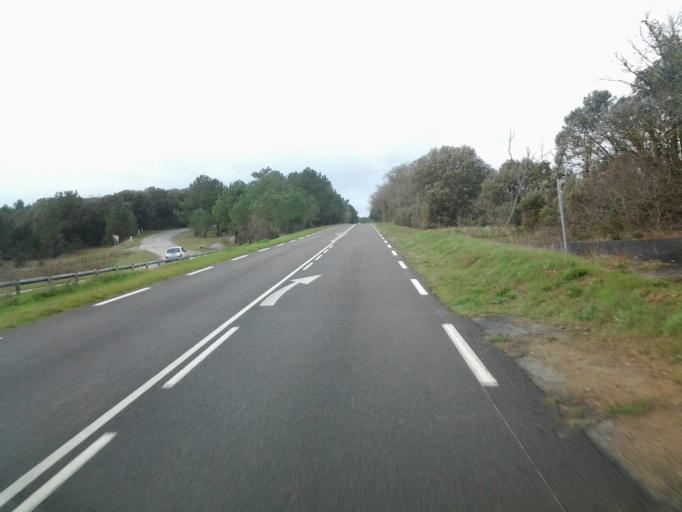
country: FR
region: Pays de la Loire
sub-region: Departement de la Vendee
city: La Tranche-sur-Mer
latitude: 46.3682
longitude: -1.4587
